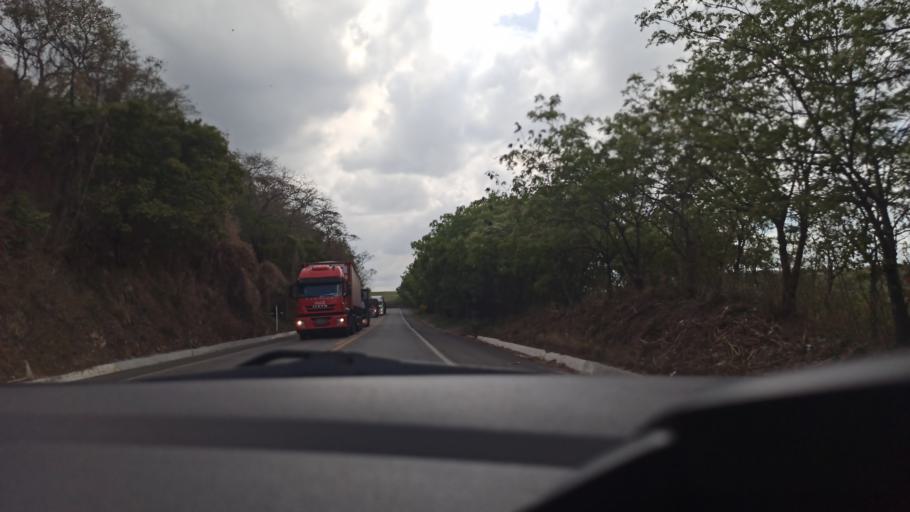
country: BR
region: Pernambuco
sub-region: Timbauba
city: Timbauba
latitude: -7.5399
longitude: -35.2810
